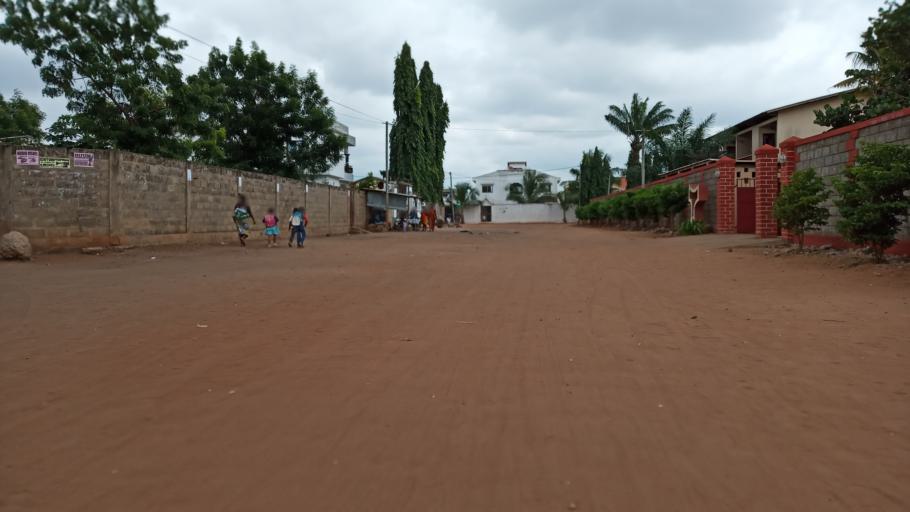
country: TG
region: Maritime
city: Lome
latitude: 6.1827
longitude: 1.1758
